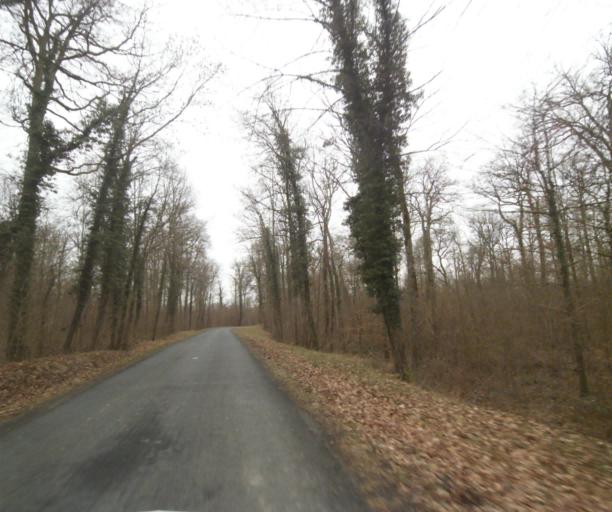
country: FR
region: Champagne-Ardenne
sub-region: Departement de la Haute-Marne
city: Bienville
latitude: 48.5667
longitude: 5.0174
